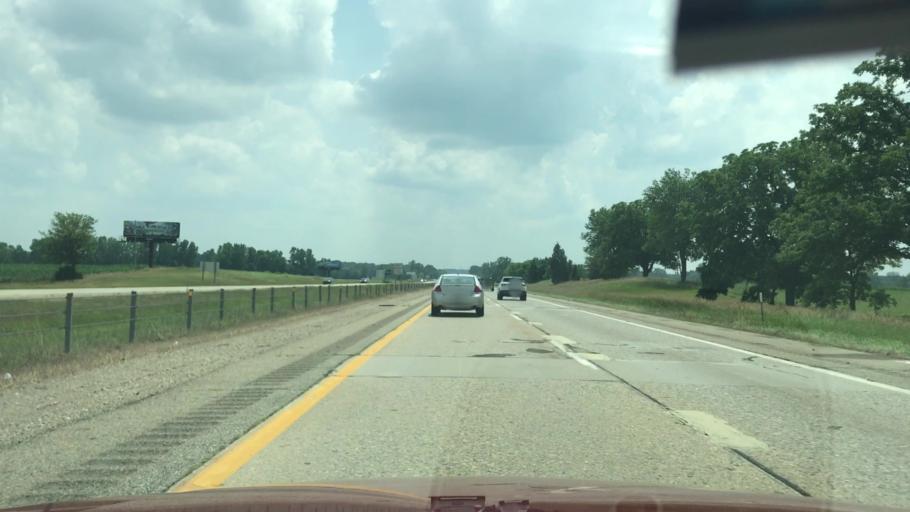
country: US
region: Michigan
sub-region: Allegan County
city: Plainwell
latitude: 42.4346
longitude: -85.6611
